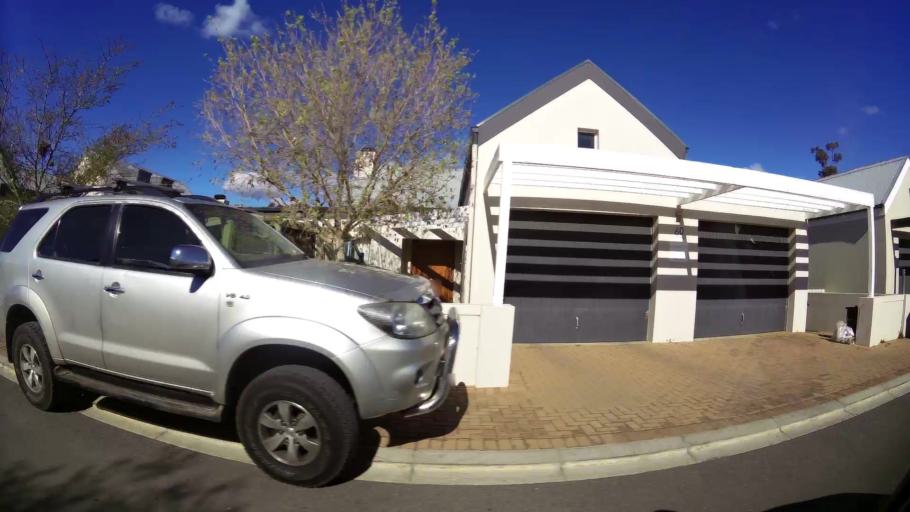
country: ZA
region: Western Cape
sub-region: Cape Winelands District Municipality
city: Ashton
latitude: -33.8130
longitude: 19.8478
